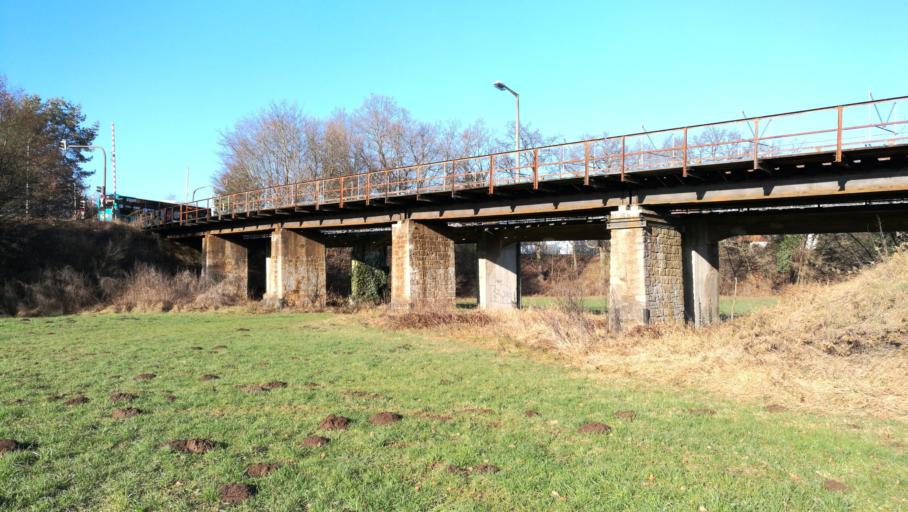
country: DE
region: Bavaria
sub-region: Regierungsbezirk Mittelfranken
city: Roth
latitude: 49.2380
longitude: 11.0844
